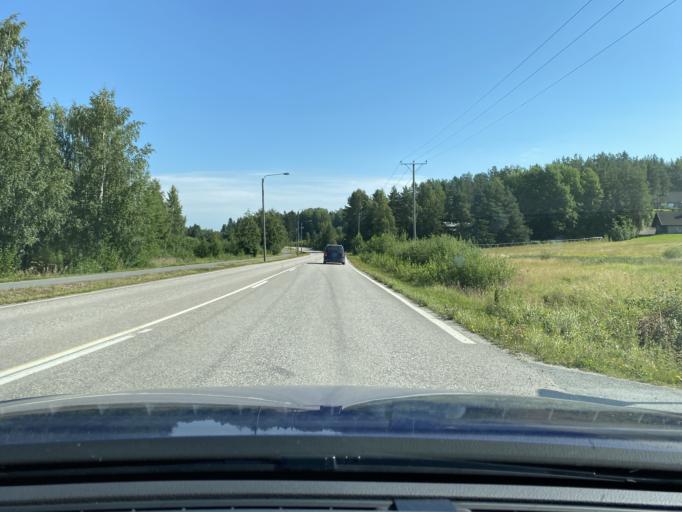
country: FI
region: Central Finland
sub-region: Jaemsae
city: Jaemsae
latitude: 61.8856
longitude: 25.2959
